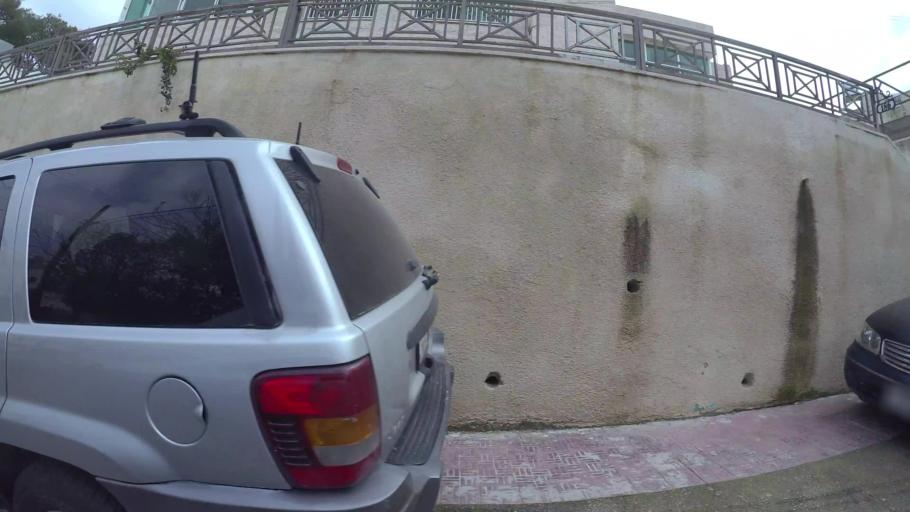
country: JO
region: Amman
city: Umm as Summaq
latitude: 31.8952
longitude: 35.8597
